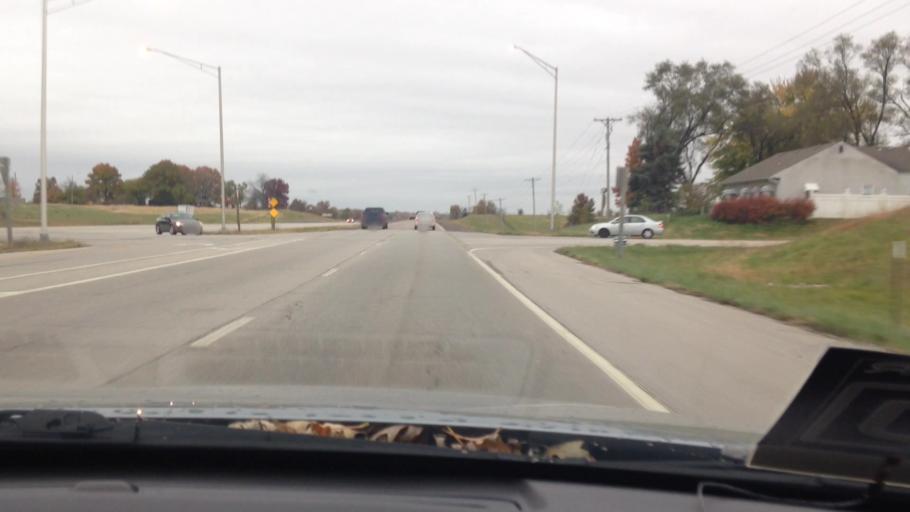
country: US
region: Kansas
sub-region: Leavenworth County
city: Basehor
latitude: 39.1583
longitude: -94.9009
